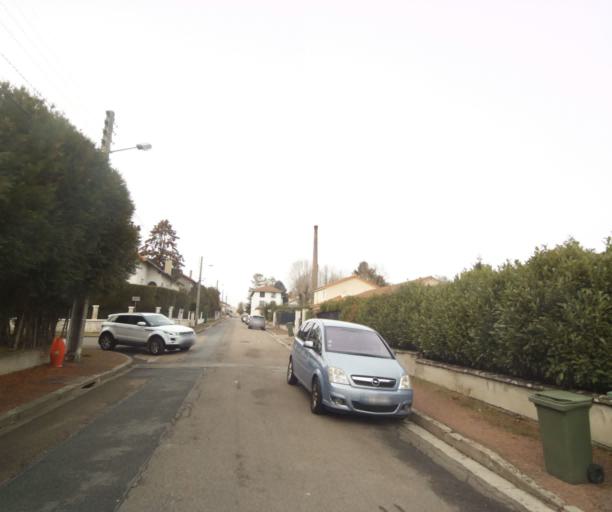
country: FR
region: Rhone-Alpes
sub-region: Departement de la Loire
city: Roanne
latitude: 46.0259
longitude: 4.0718
